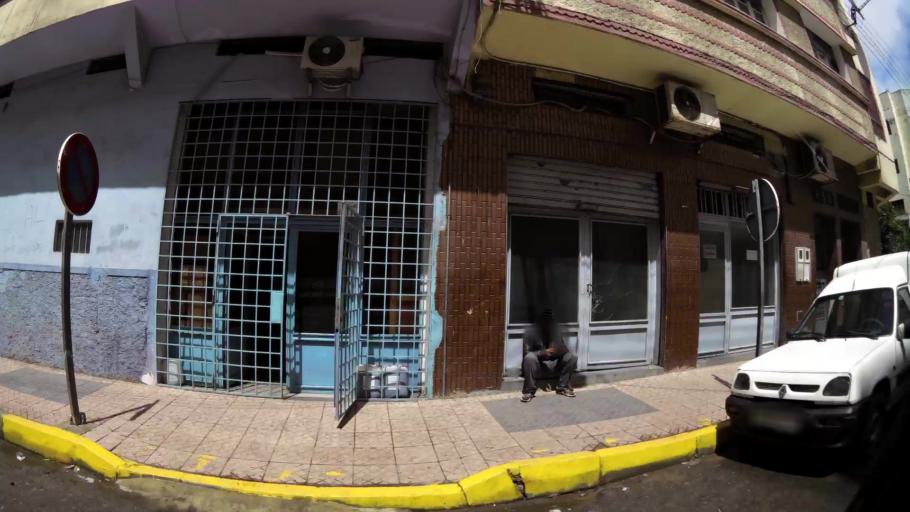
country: MA
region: Grand Casablanca
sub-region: Casablanca
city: Casablanca
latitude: 33.5778
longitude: -7.5899
